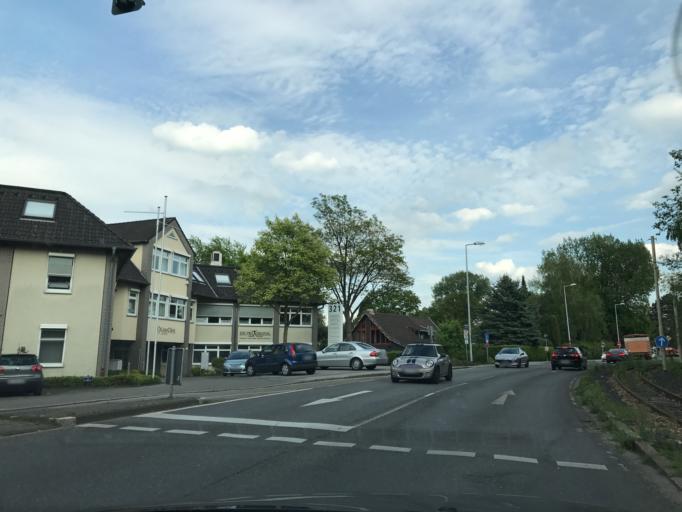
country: DE
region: North Rhine-Westphalia
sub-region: Regierungsbezirk Dusseldorf
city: Muelheim (Ruhr)
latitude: 51.4086
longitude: 6.9361
